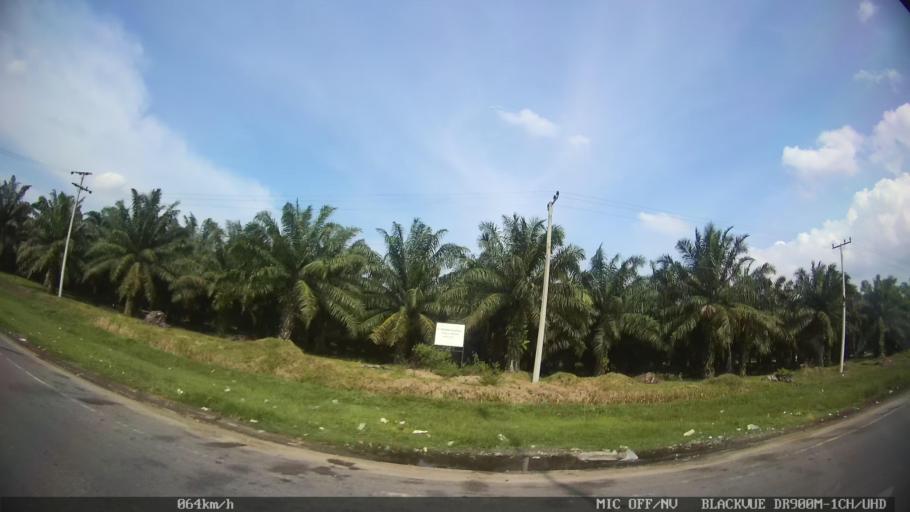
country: ID
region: North Sumatra
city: Binjai
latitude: 3.6484
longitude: 98.5356
